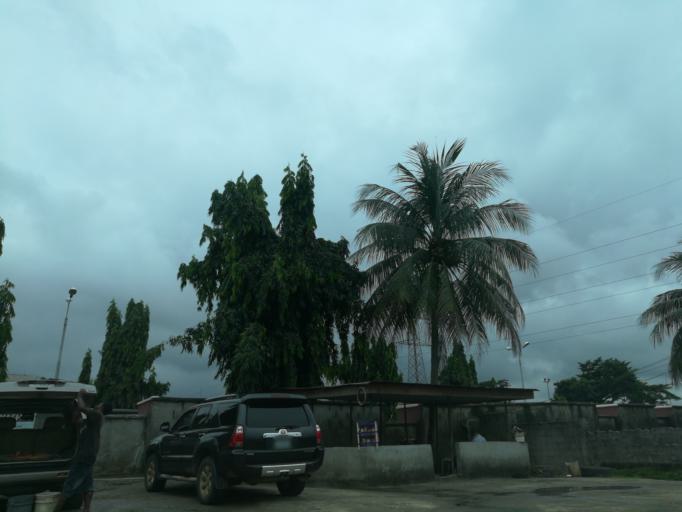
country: NG
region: Rivers
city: Port Harcourt
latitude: 4.8338
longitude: 7.0300
